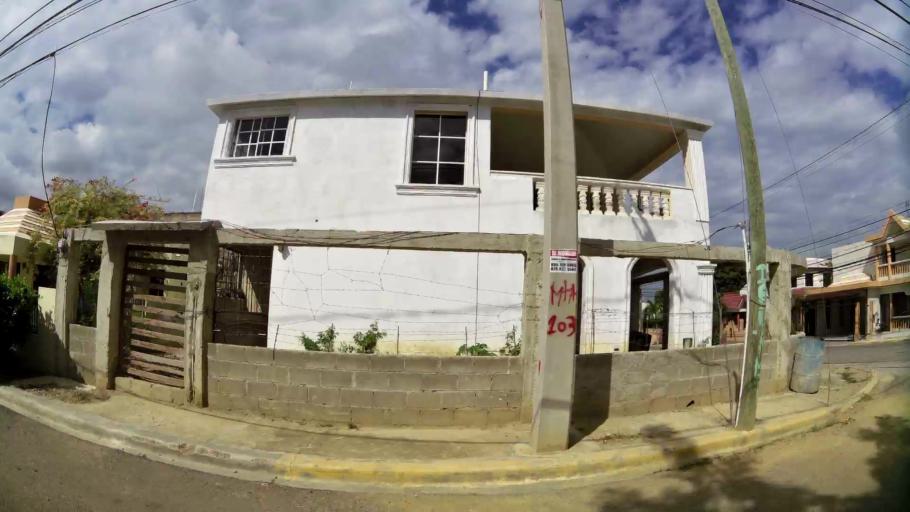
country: DO
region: Santiago
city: Santiago de los Caballeros
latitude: 19.4887
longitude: -70.7296
